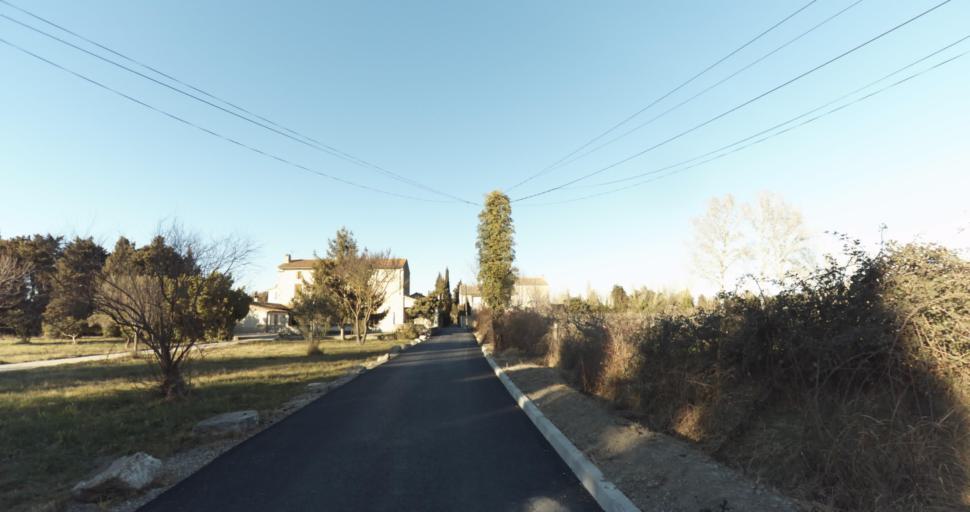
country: FR
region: Provence-Alpes-Cote d'Azur
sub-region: Departement des Bouches-du-Rhone
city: Barbentane
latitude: 43.9025
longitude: 4.7438
